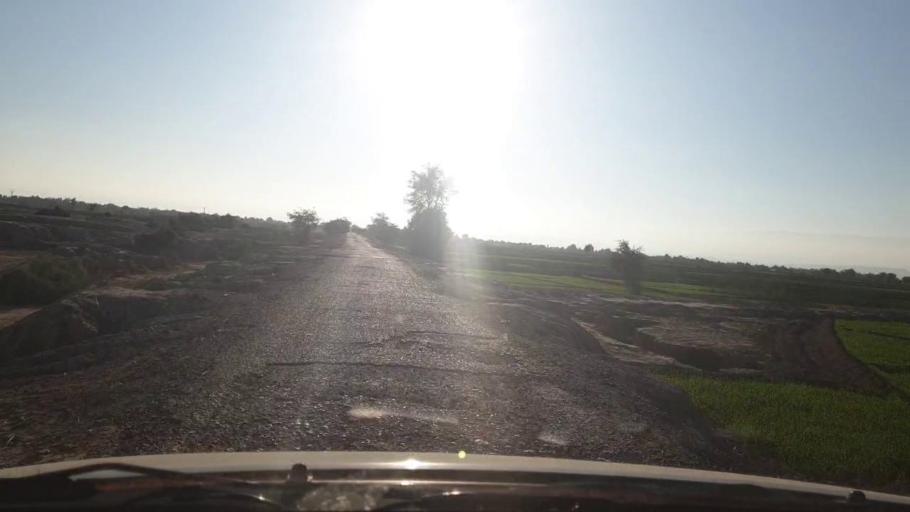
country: PK
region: Sindh
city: Johi
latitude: 26.7722
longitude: 67.4487
